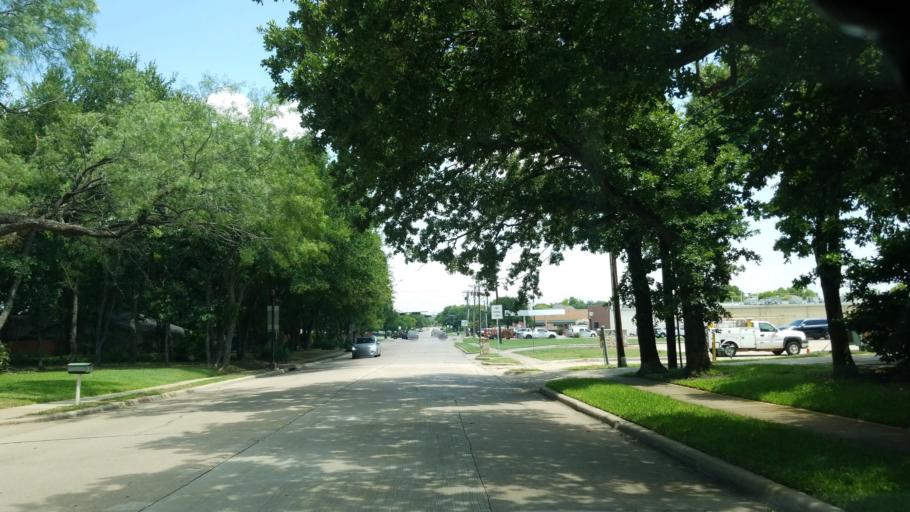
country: US
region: Texas
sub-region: Dallas County
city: Coppell
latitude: 32.9678
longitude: -96.9766
